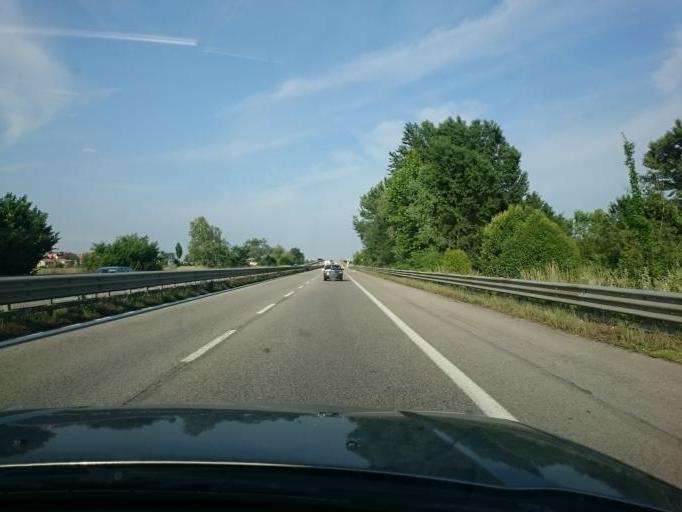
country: IT
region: Veneto
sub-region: Provincia di Padova
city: Albignasego
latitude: 45.3663
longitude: 11.8816
